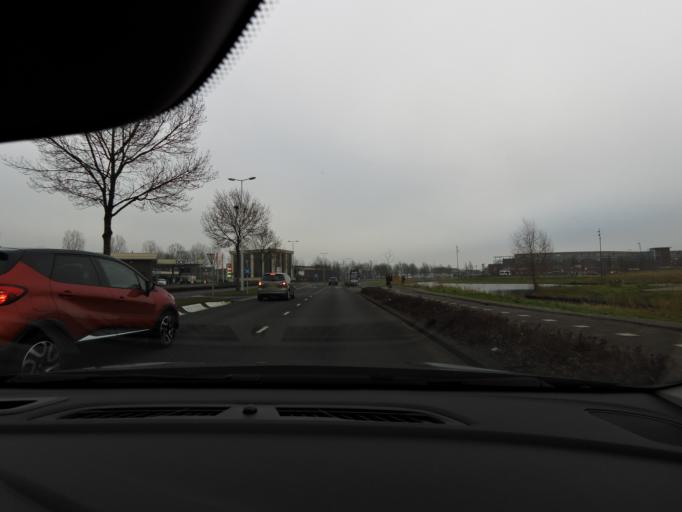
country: NL
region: South Holland
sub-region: Gemeente Spijkenisse
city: Spijkenisse
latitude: 51.8416
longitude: 4.3468
